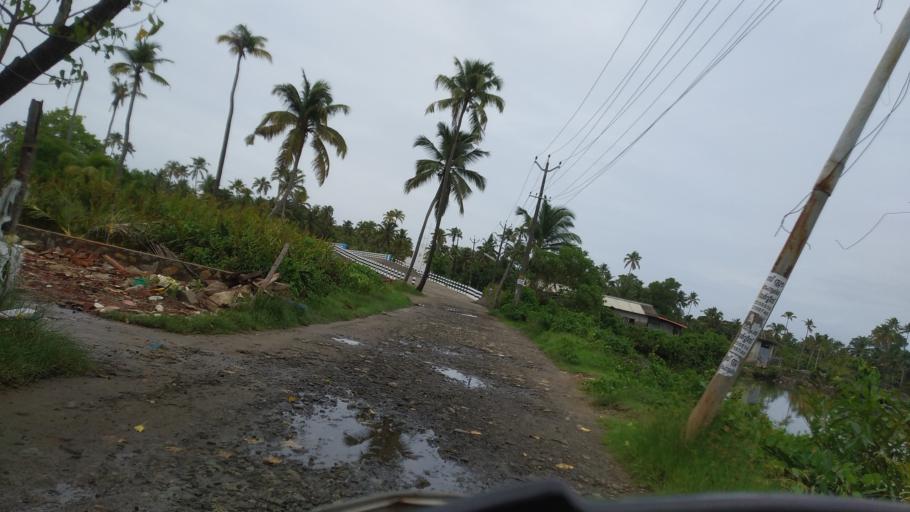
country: IN
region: Kerala
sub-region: Ernakulam
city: Elur
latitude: 10.0683
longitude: 76.2193
